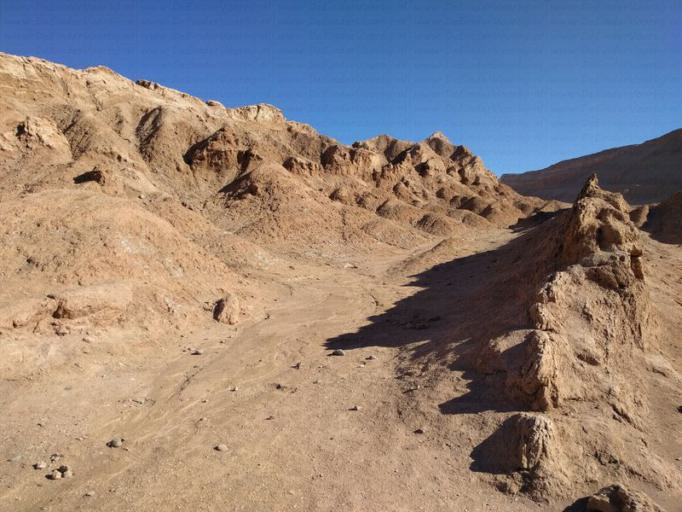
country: CL
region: Antofagasta
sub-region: Provincia de El Loa
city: San Pedro de Atacama
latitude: -22.9013
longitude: -68.2378
